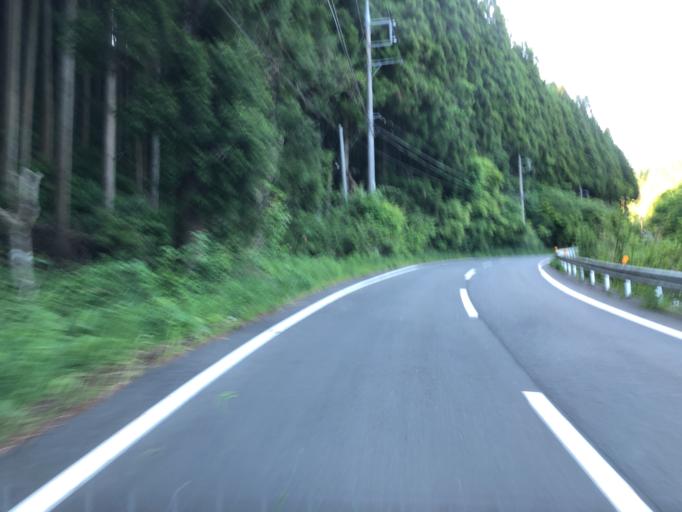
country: JP
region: Ibaraki
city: Kitaibaraki
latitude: 36.8659
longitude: 140.6368
